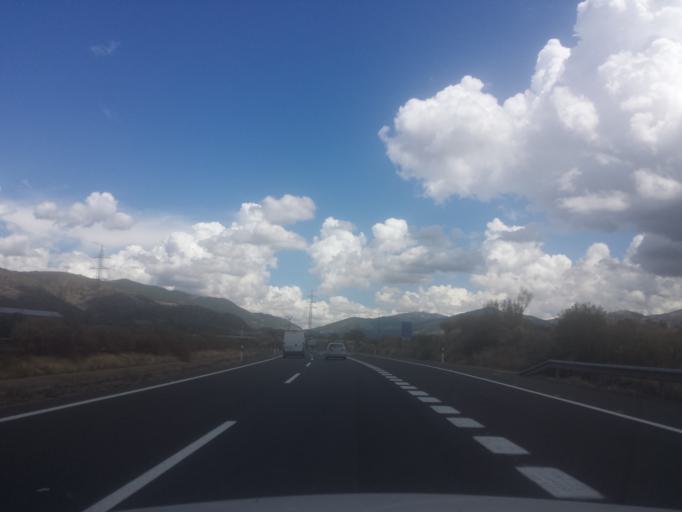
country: ES
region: Extremadura
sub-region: Provincia de Caceres
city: Aldeanueva del Camino
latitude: 40.2600
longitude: -5.9174
